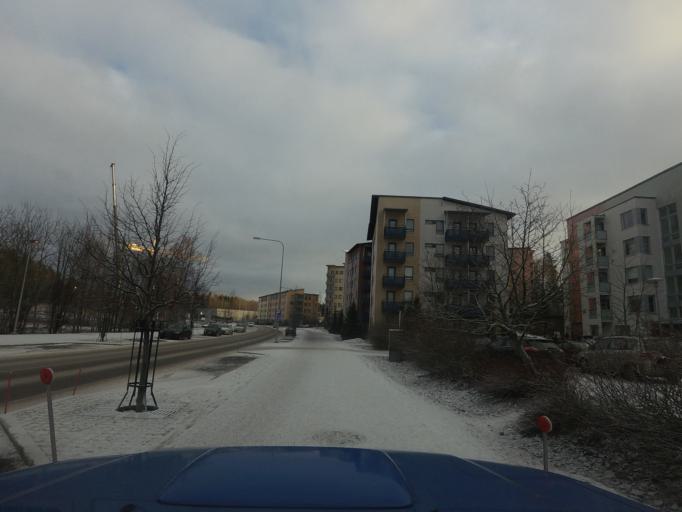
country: FI
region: Uusimaa
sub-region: Helsinki
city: Kauniainen
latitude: 60.2058
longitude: 24.7054
